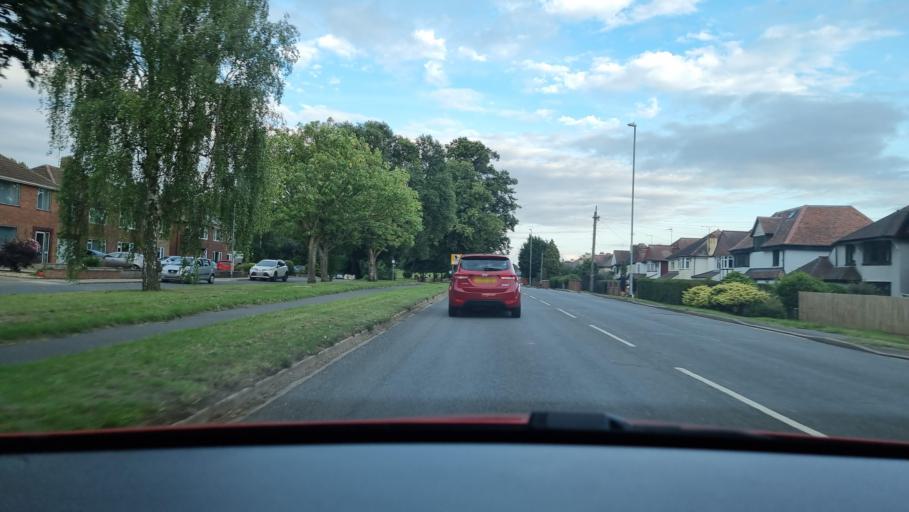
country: GB
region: England
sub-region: Northamptonshire
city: Northampton
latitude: 52.2671
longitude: -0.9075
